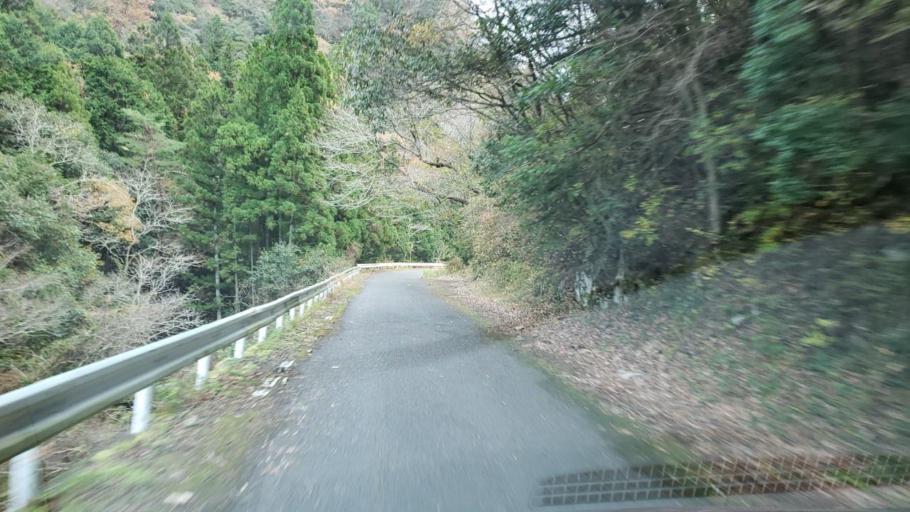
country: JP
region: Tokushima
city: Wakimachi
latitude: 34.1455
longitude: 134.2286
